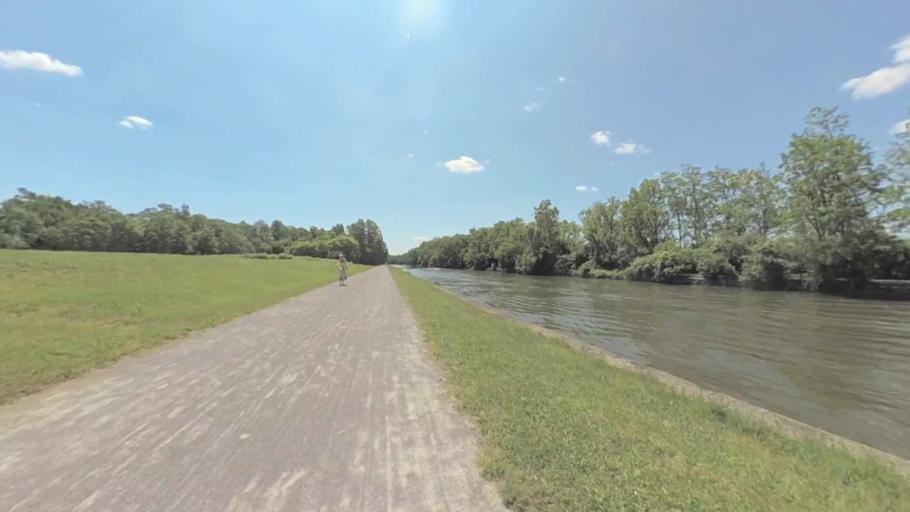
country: US
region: New York
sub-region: Monroe County
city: Pittsford
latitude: 43.0711
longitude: -77.4911
